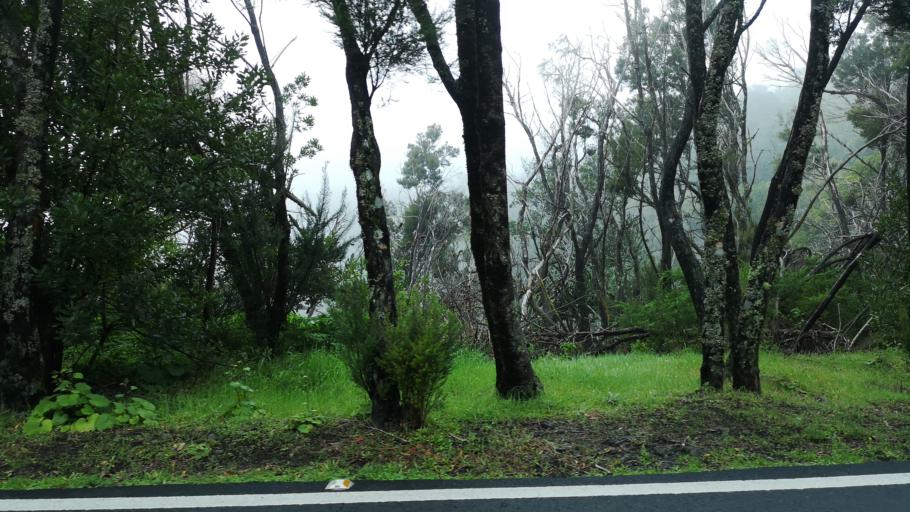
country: ES
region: Canary Islands
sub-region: Provincia de Santa Cruz de Tenerife
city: Vallehermosa
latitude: 28.1280
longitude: -17.2678
